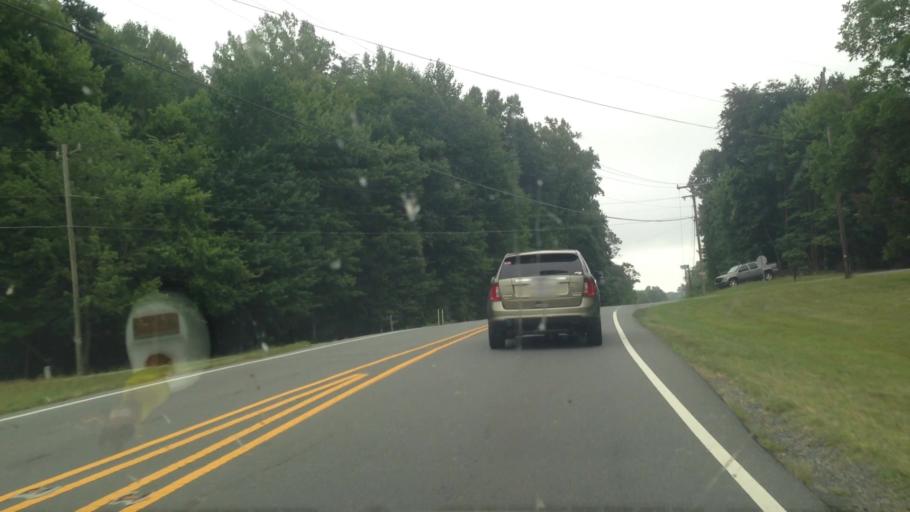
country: US
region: North Carolina
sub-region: Forsyth County
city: Walkertown
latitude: 36.1628
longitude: -80.1332
